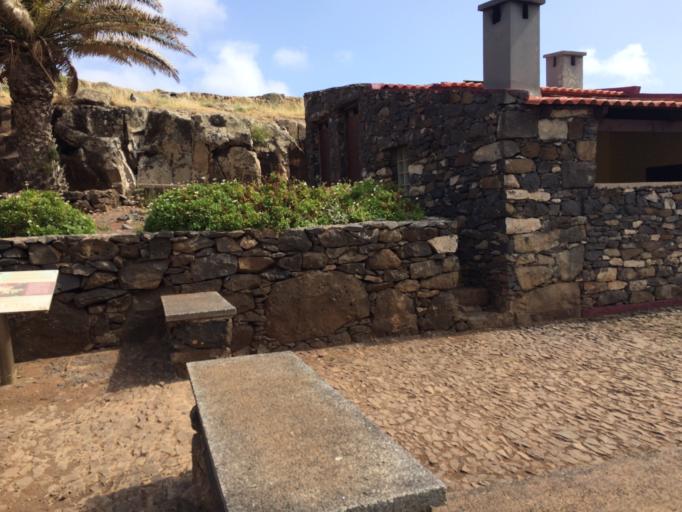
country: PT
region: Madeira
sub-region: Machico
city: Canical
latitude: 32.7423
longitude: -16.6833
